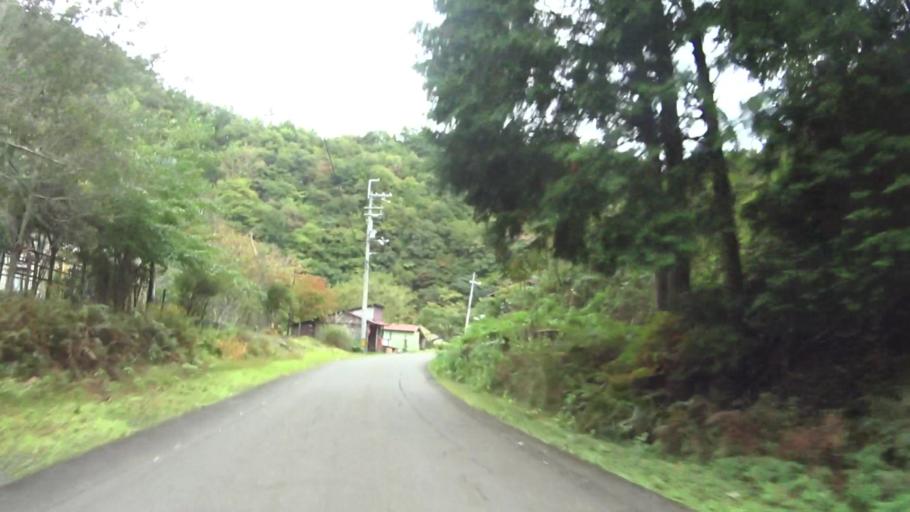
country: JP
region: Fukui
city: Obama
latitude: 35.2934
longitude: 135.6941
